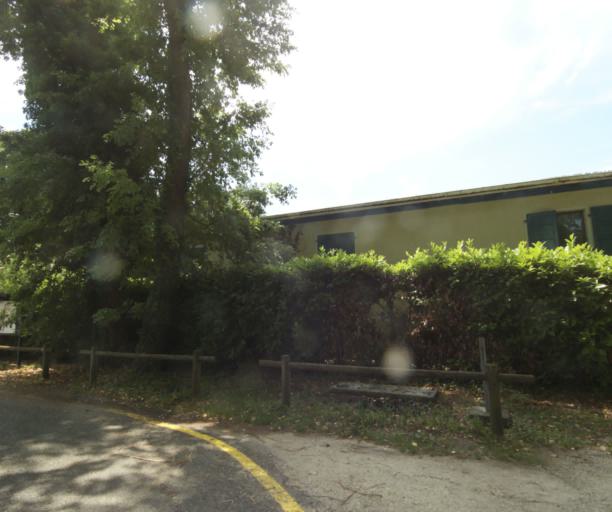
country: FR
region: Rhone-Alpes
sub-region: Departement de la Haute-Savoie
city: Chens-sur-Leman
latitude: 46.3238
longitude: 6.2574
